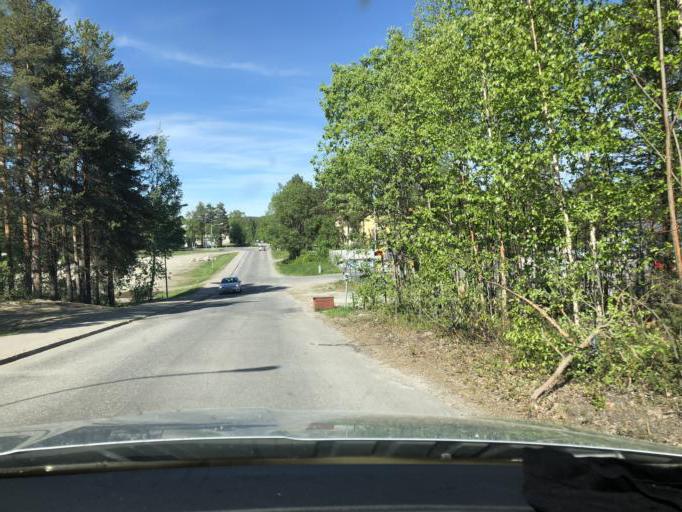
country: SE
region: Norrbotten
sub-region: Jokkmokks Kommun
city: Jokkmokk
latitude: 66.6021
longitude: 19.8463
